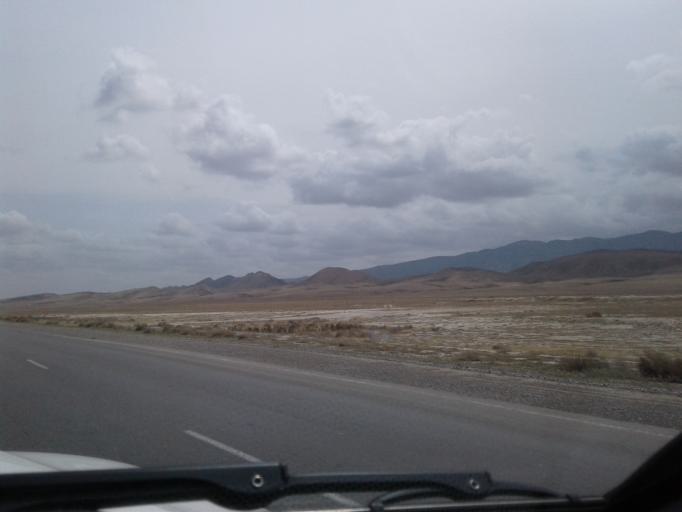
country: IR
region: Razavi Khorasan
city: Dargaz
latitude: 37.7012
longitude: 59.0419
